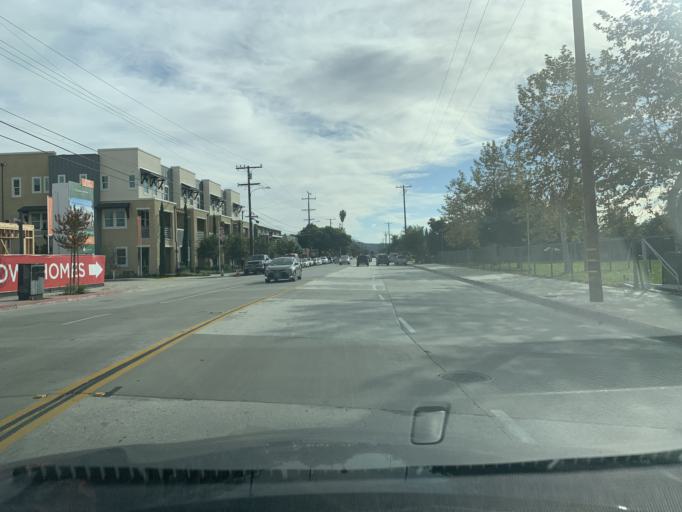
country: US
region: California
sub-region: Los Angeles County
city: South El Monte
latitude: 34.0618
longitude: -118.0424
